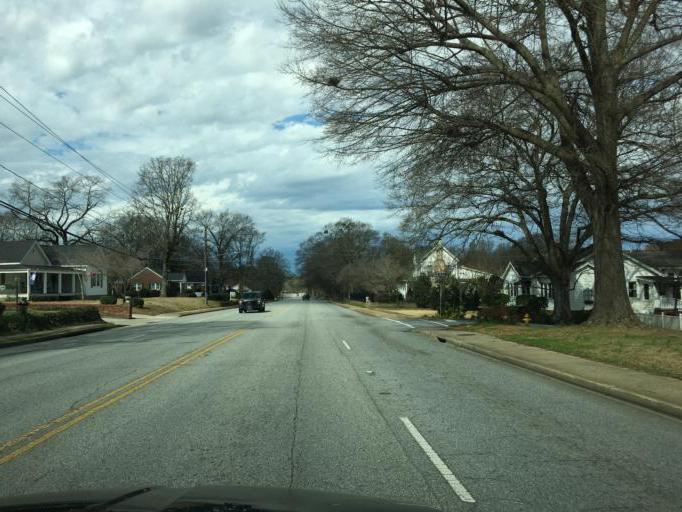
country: US
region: South Carolina
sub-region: Greenville County
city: Fountain Inn
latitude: 34.6984
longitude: -82.2071
